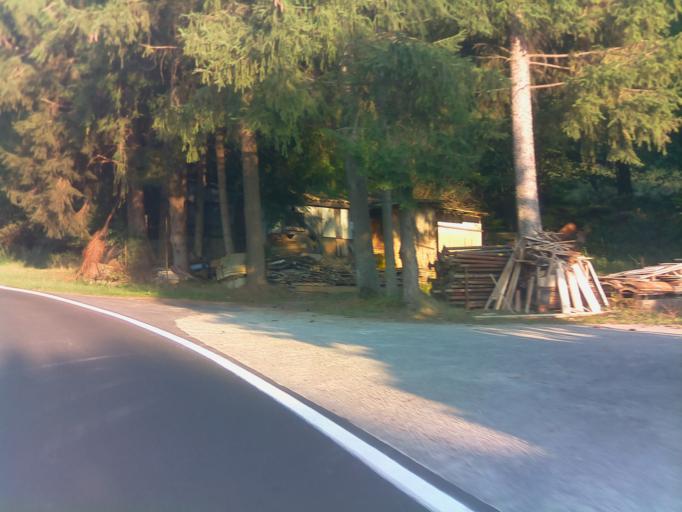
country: DE
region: Bavaria
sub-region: Regierungsbezirk Unterfranken
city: Burgsinn
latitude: 50.1582
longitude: 9.6562
